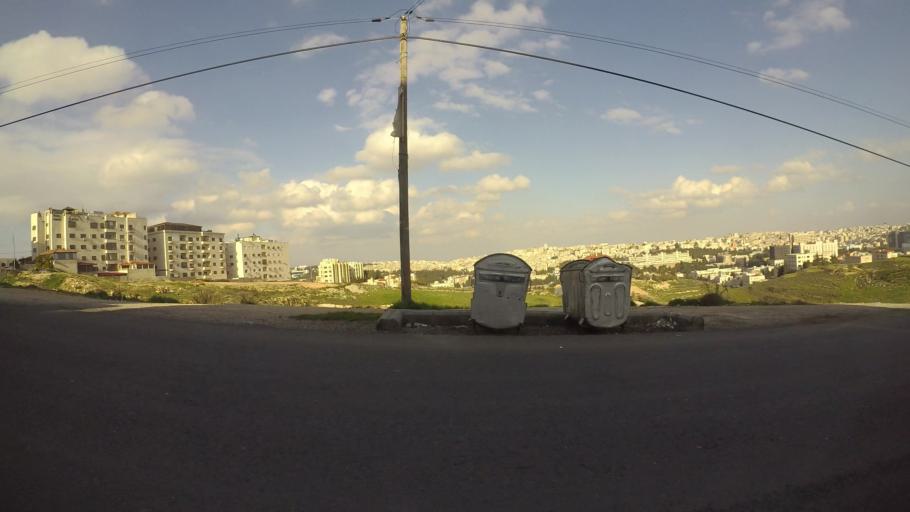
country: JO
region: Amman
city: Al Jubayhah
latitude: 32.0099
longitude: 35.8641
